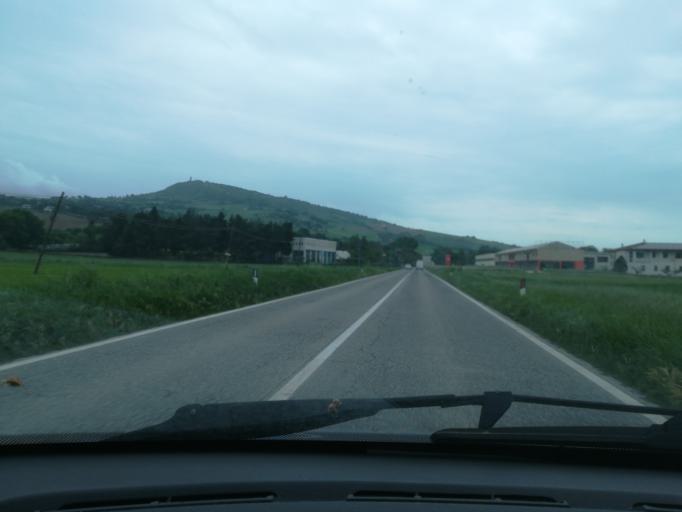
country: IT
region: The Marches
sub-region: Provincia di Macerata
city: San Severino Marche
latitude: 43.2547
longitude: 13.2324
